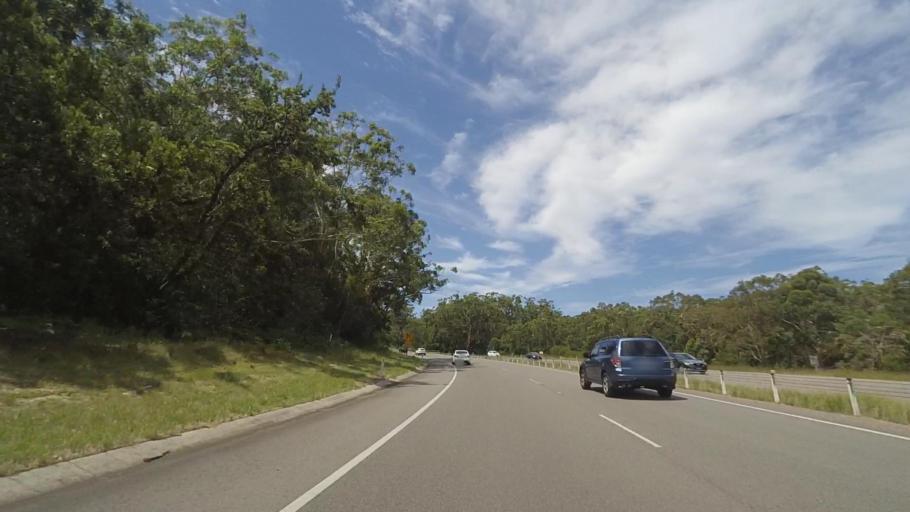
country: AU
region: New South Wales
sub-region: Port Stephens Shire
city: Anna Bay
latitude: -32.7721
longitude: 152.0108
